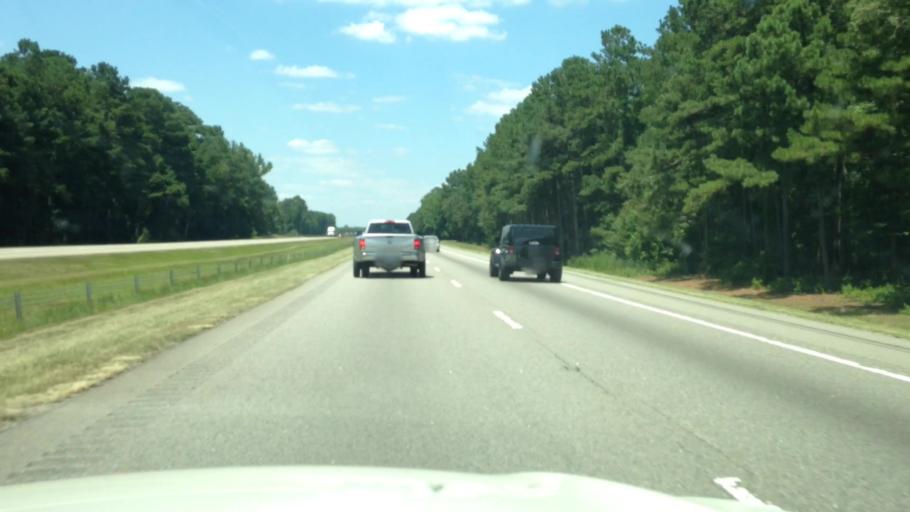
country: US
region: North Carolina
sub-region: Robeson County
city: Saint Pauls
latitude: 34.7792
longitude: -78.9954
